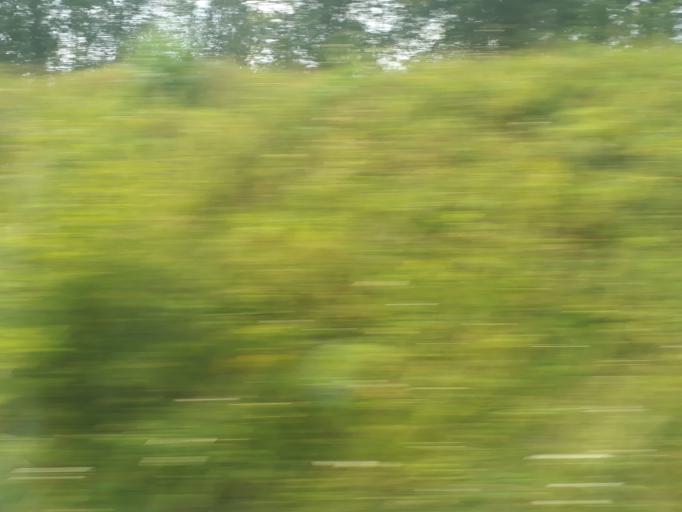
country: EE
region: Laeaene-Virumaa
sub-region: Rakke vald
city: Rakke
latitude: 59.0369
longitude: 26.2366
